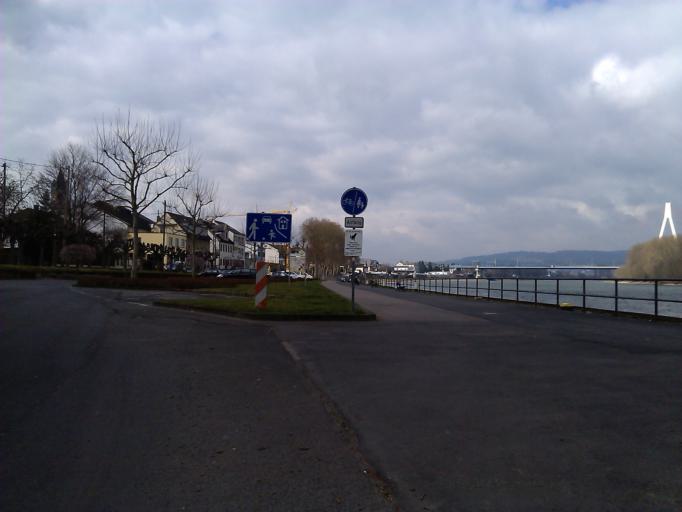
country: DE
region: Rheinland-Pfalz
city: Kettig
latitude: 50.4135
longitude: 7.4653
